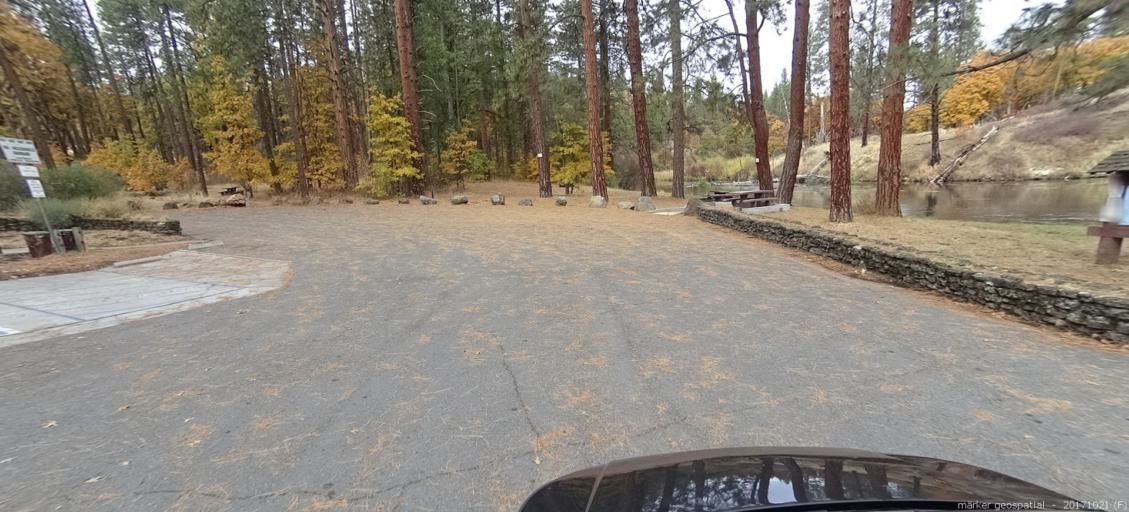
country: US
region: California
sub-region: Shasta County
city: Burney
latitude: 40.9771
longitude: -121.5578
